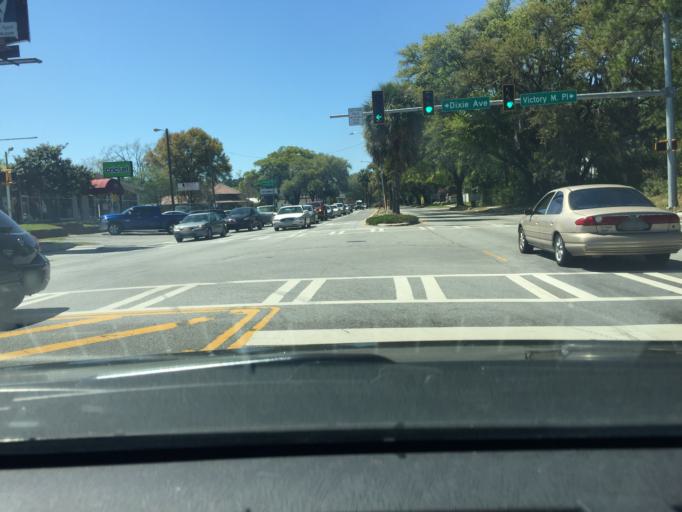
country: US
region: Georgia
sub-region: Chatham County
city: Thunderbolt
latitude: 32.0446
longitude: -81.0721
